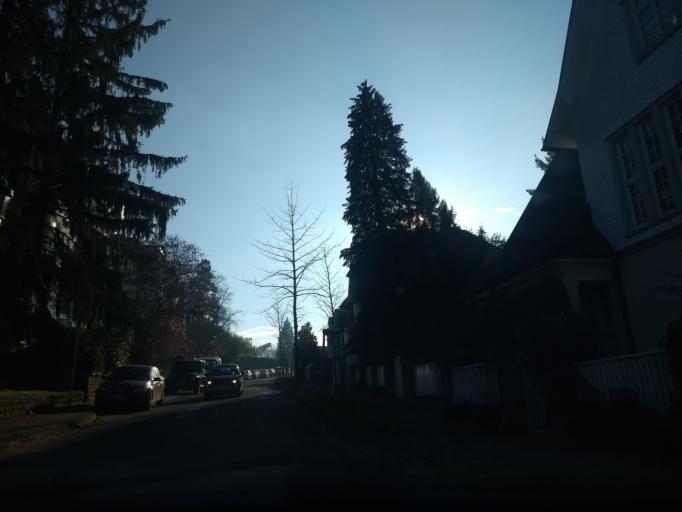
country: DE
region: Baden-Wuerttemberg
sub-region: Karlsruhe Region
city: Baden-Baden
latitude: 48.7620
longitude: 8.2497
